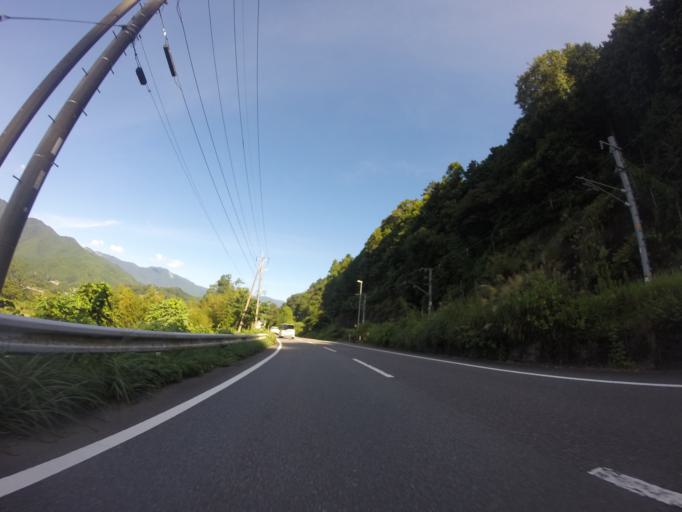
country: JP
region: Shizuoka
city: Fujinomiya
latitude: 35.2629
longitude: 138.4775
